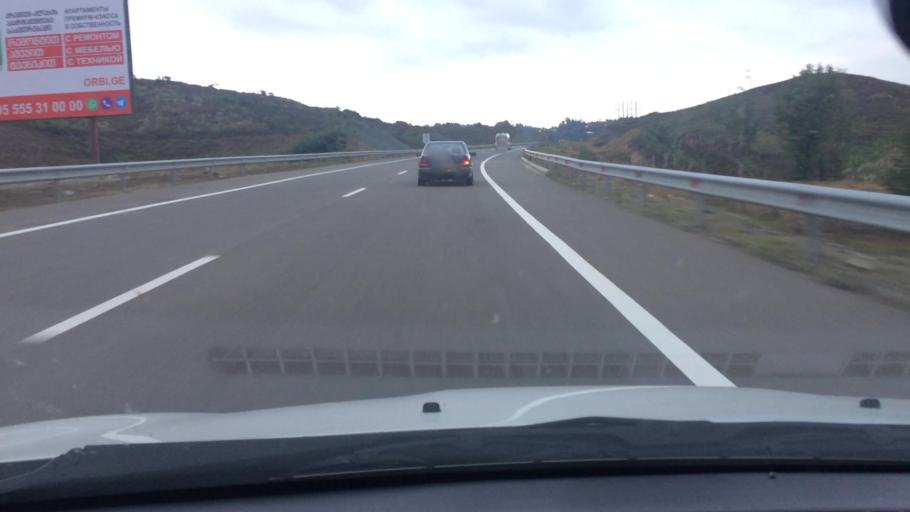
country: GE
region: Ajaria
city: Makhinjauri
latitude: 41.7252
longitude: 41.7496
